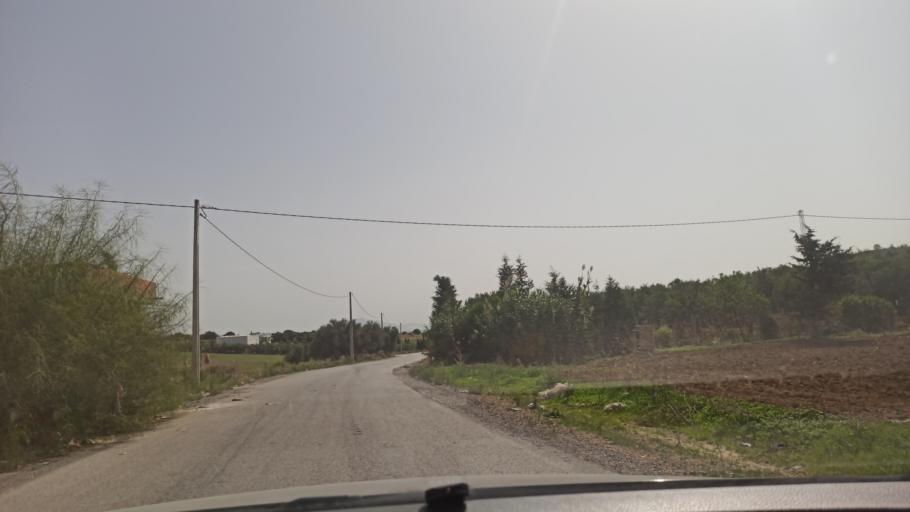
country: TN
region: Manouba
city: Manouba
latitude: 36.7320
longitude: 10.0935
